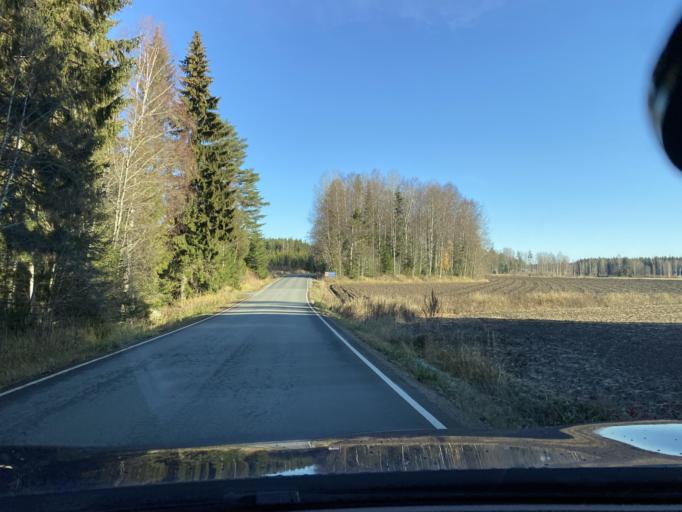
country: FI
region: Haeme
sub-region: Haemeenlinna
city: Kalvola
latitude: 61.0238
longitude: 24.1592
